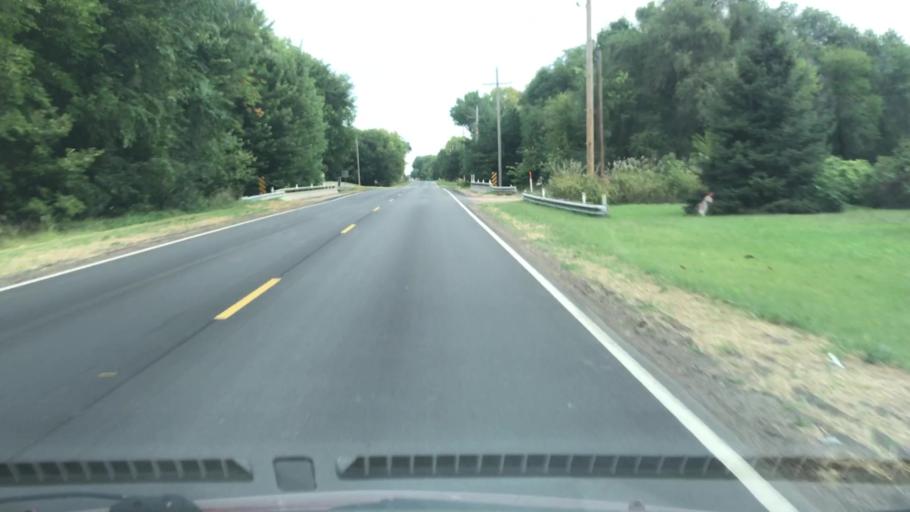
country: US
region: Nebraska
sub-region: Hall County
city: Grand Island
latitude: 40.9203
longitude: -98.3016
